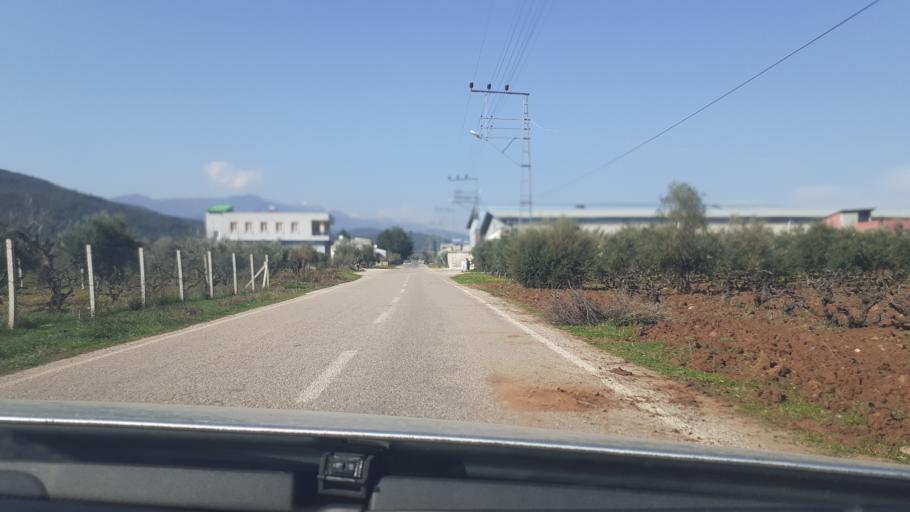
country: TR
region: Hatay
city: Aktepe
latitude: 36.7122
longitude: 36.4859
